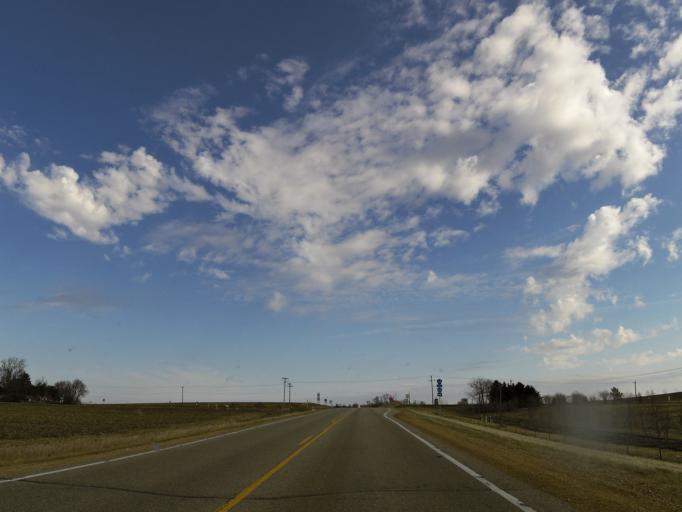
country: US
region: Minnesota
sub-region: Washington County
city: Cottage Grove
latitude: 44.8462
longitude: -92.8626
